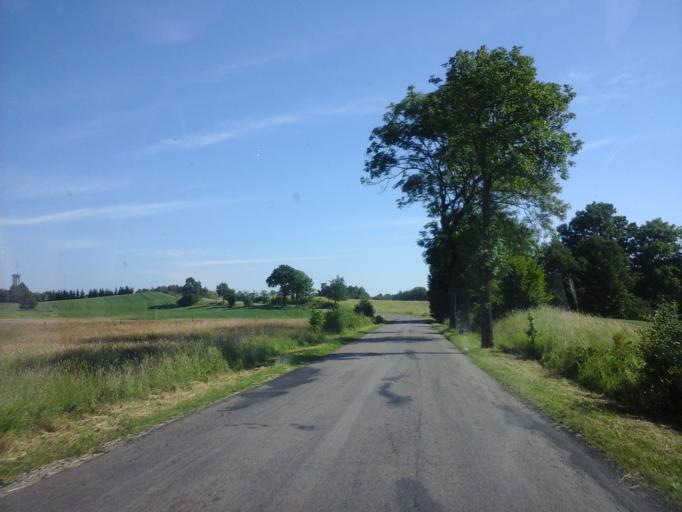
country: PL
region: West Pomeranian Voivodeship
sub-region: Powiat swidwinski
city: Polczyn-Zdroj
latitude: 53.7071
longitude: 16.0657
